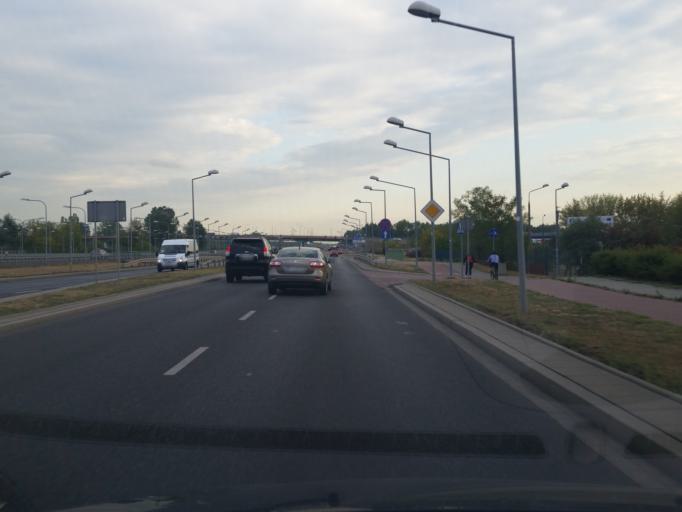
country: PL
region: Masovian Voivodeship
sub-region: Warszawa
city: Wlochy
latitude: 52.1603
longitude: 20.9863
